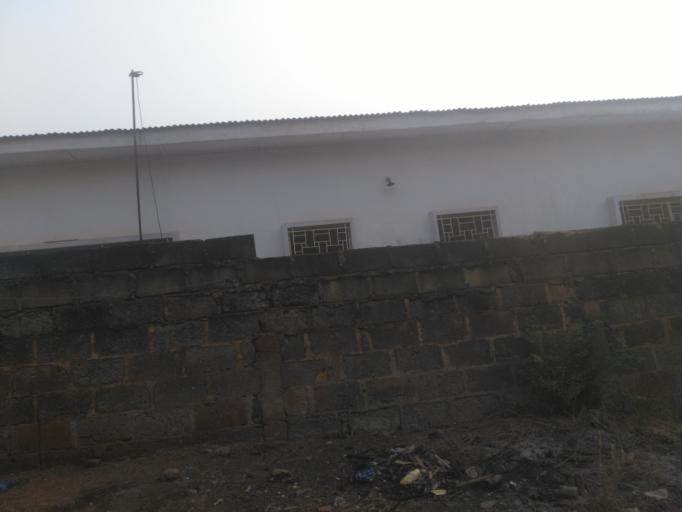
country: GH
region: Ashanti
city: Kumasi
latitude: 6.6695
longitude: -1.6053
